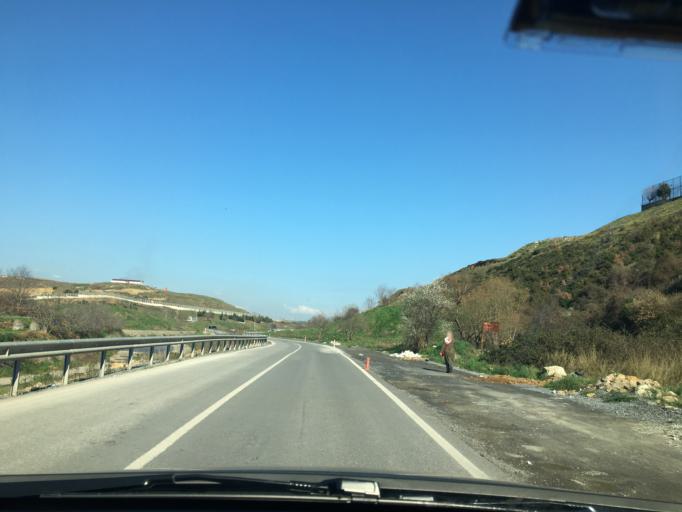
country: TR
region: Istanbul
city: Pendik
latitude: 40.8723
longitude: 29.2935
